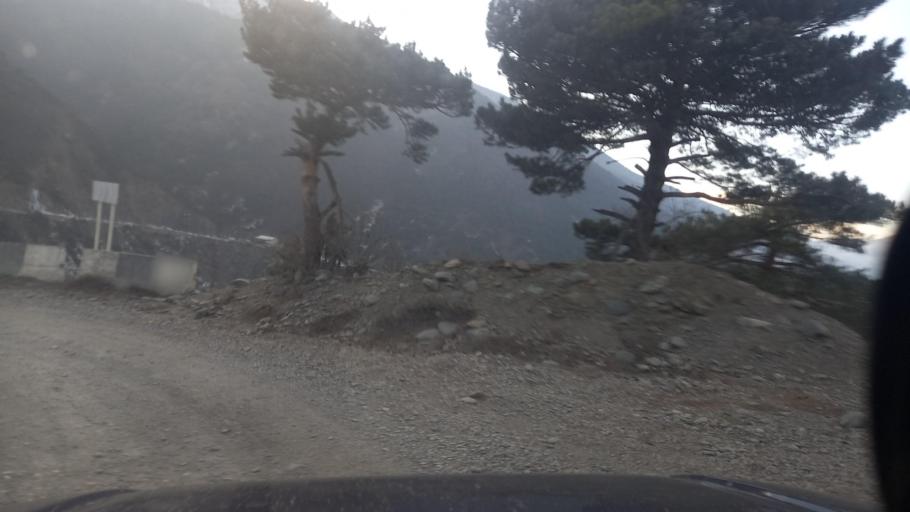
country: RU
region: Ingushetiya
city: Dzhayrakh
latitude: 42.8183
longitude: 44.7018
